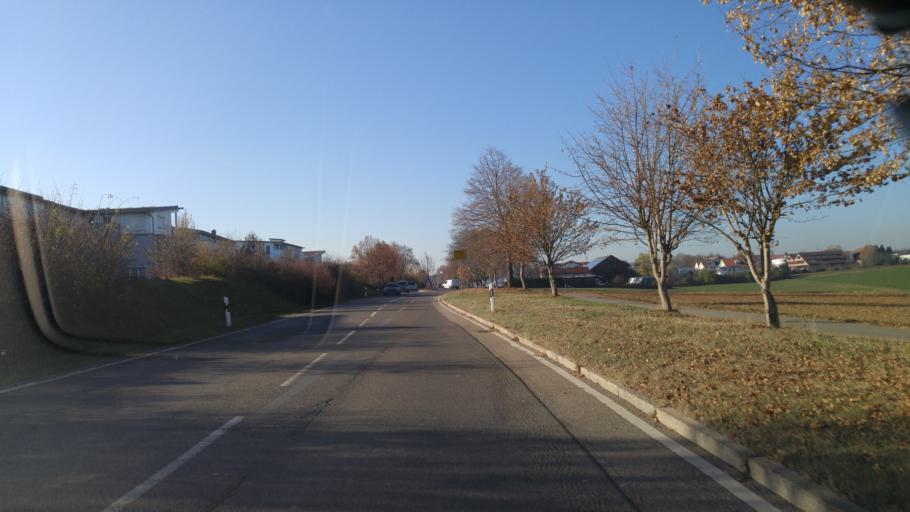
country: DE
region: Baden-Wuerttemberg
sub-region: Regierungsbezirk Stuttgart
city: Leonberg
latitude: 48.8179
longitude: 9.0339
